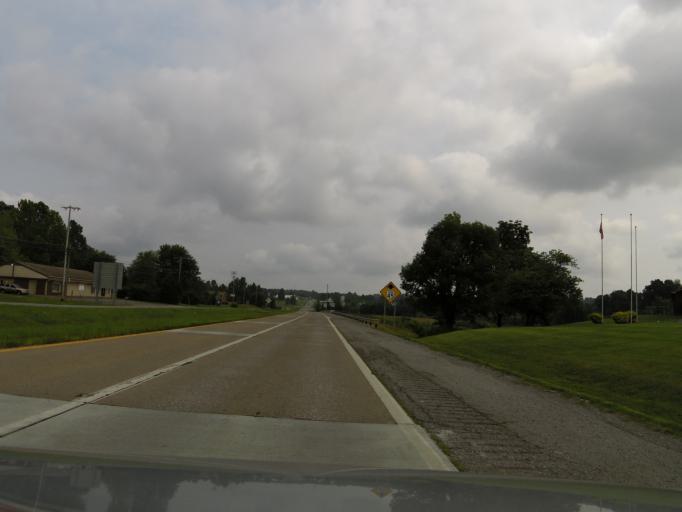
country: US
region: Kentucky
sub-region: Hopkins County
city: Madisonville
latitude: 37.3724
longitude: -87.4913
